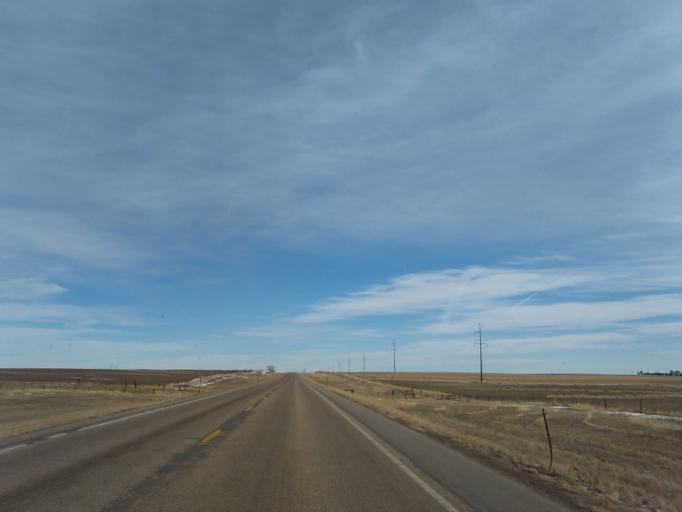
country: US
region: Wyoming
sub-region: Laramie County
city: Pine Bluffs
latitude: 41.4218
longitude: -104.4013
